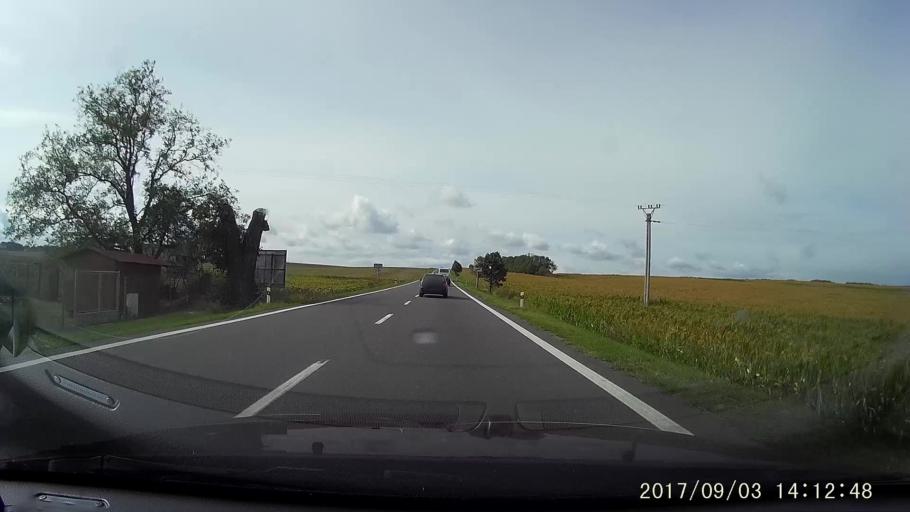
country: CZ
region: South Moravian
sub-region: Okres Znojmo
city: Znojmo
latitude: 48.8734
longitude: 16.0235
